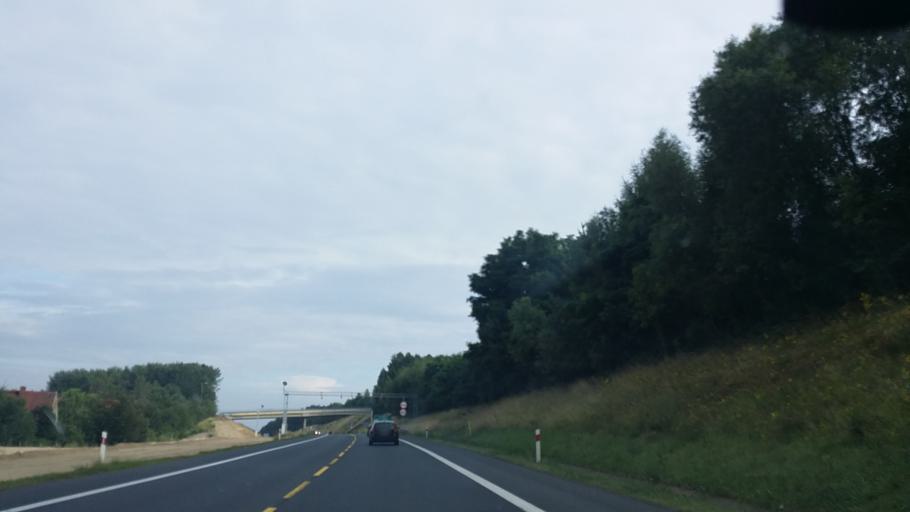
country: PL
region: Lubusz
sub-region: Zielona Gora
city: Zielona Gora
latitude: 51.9331
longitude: 15.5508
